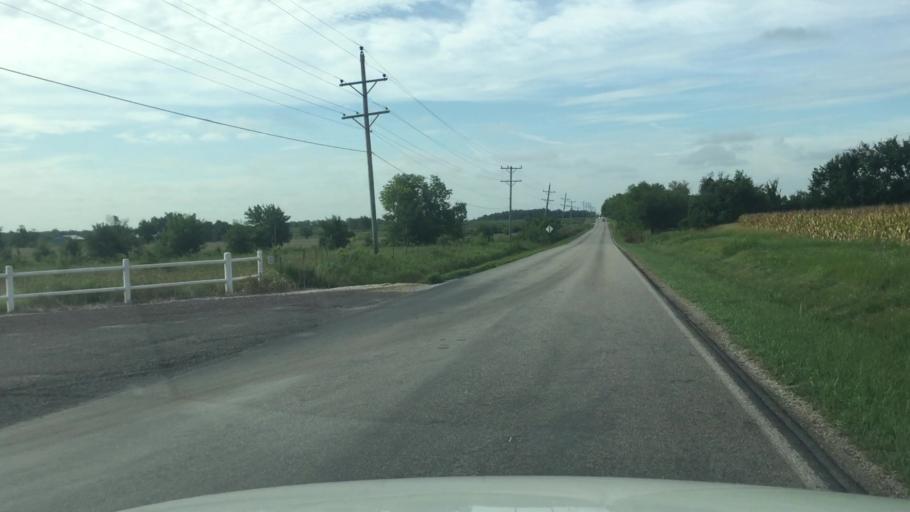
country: US
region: Kansas
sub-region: Allen County
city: Humboldt
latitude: 37.8540
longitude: -95.4369
